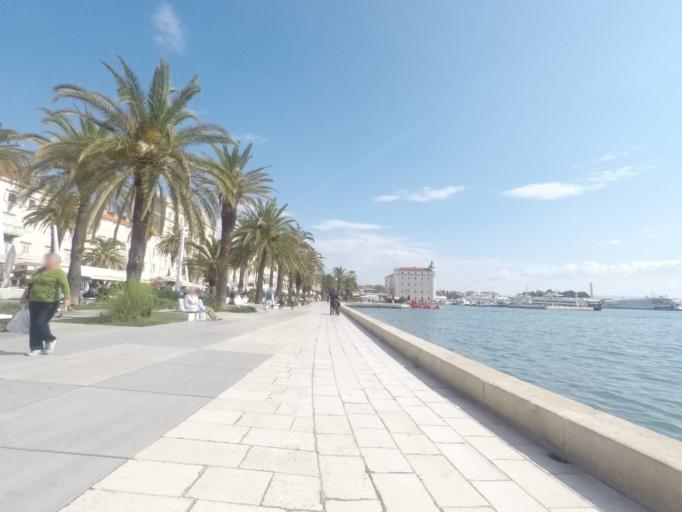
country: HR
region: Splitsko-Dalmatinska
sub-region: Grad Split
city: Split
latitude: 43.5080
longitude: 16.4369
